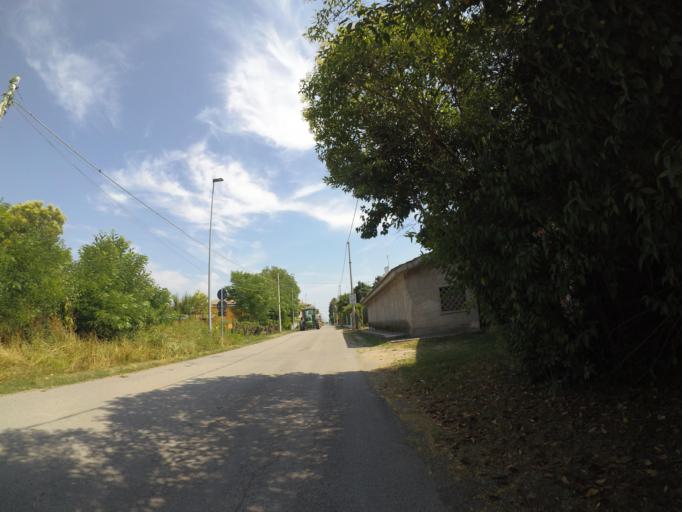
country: IT
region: Friuli Venezia Giulia
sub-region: Provincia di Pordenone
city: Rosa
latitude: 45.9258
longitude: 12.8835
